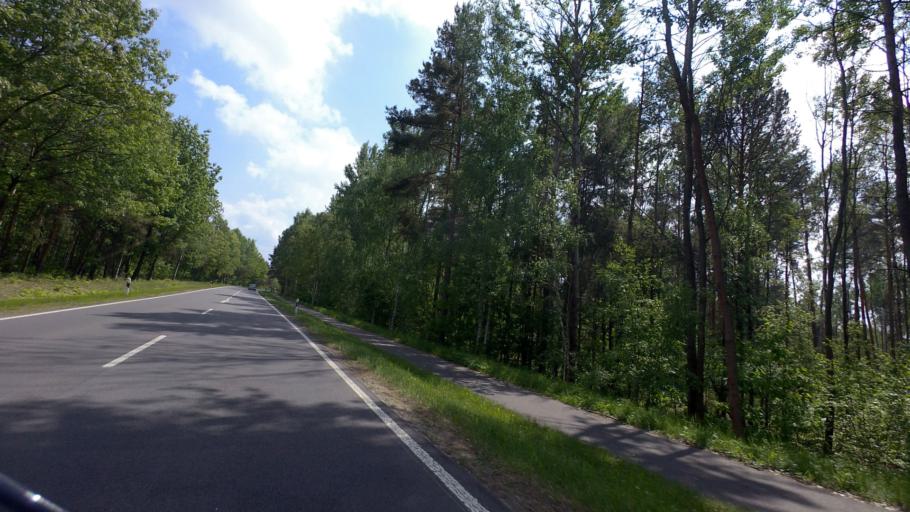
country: DE
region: Saxony
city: Trebendorf
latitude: 51.5277
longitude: 14.6015
